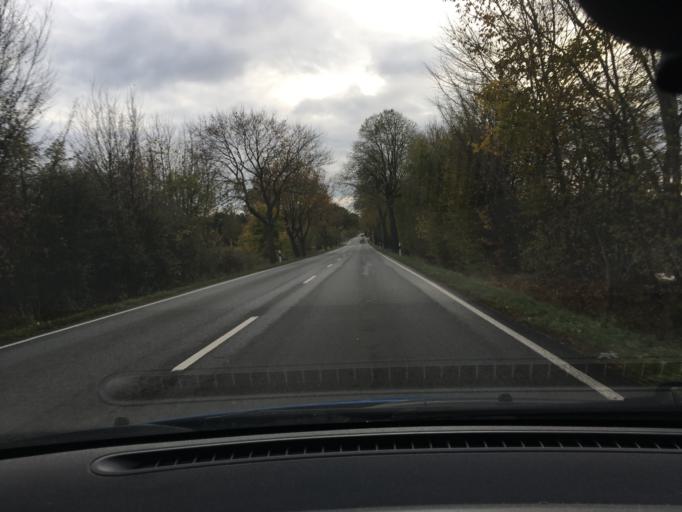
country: DE
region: Schleswig-Holstein
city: Talkau
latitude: 53.5731
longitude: 10.5670
